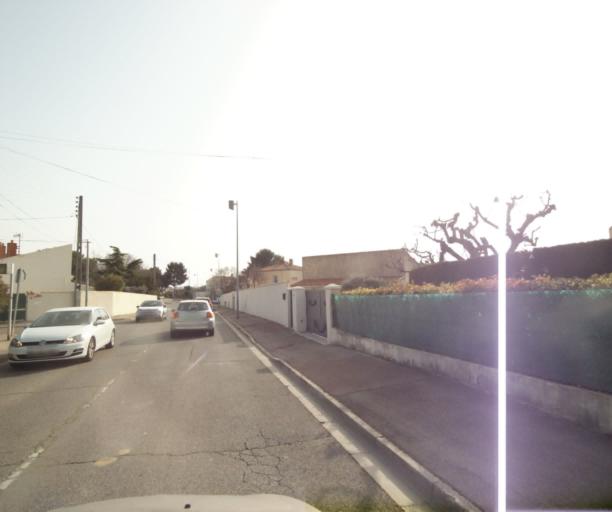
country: FR
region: Provence-Alpes-Cote d'Azur
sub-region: Departement des Bouches-du-Rhone
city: Vitrolles
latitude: 43.4553
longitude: 5.2428
